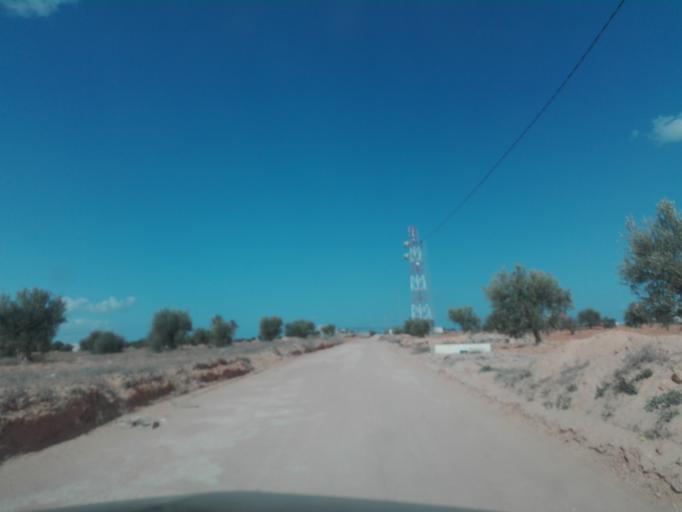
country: TN
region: Madanin
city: Bin Qirdan
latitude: 33.1670
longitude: 11.1965
